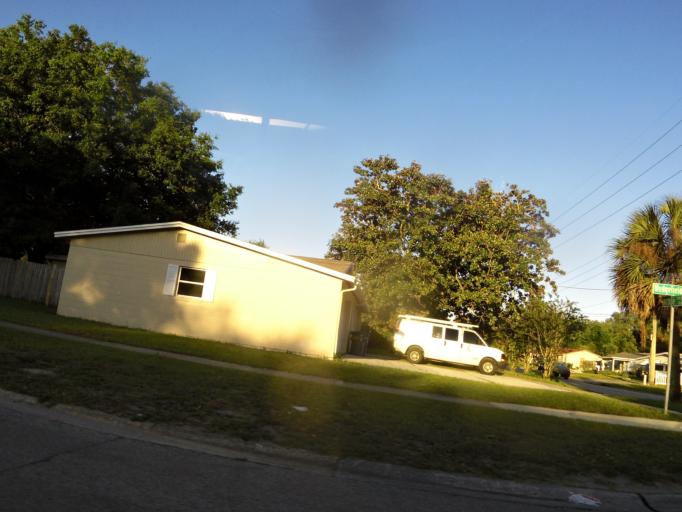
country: US
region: Florida
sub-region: Duval County
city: Jacksonville
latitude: 30.3456
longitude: -81.5686
